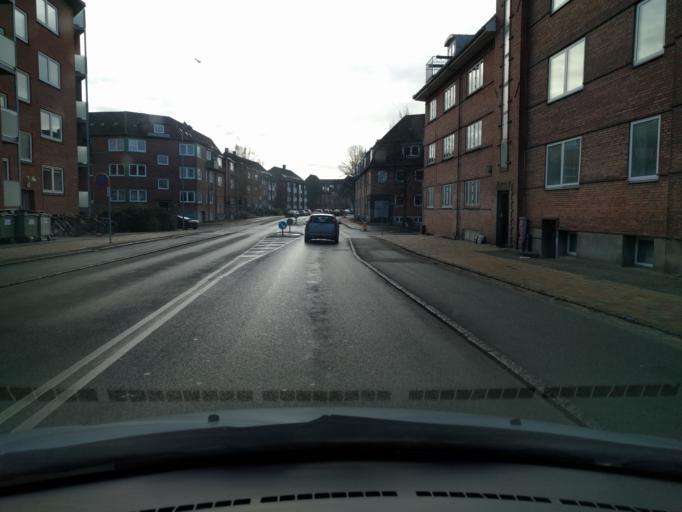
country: DK
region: South Denmark
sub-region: Odense Kommune
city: Odense
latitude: 55.3968
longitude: 10.4058
